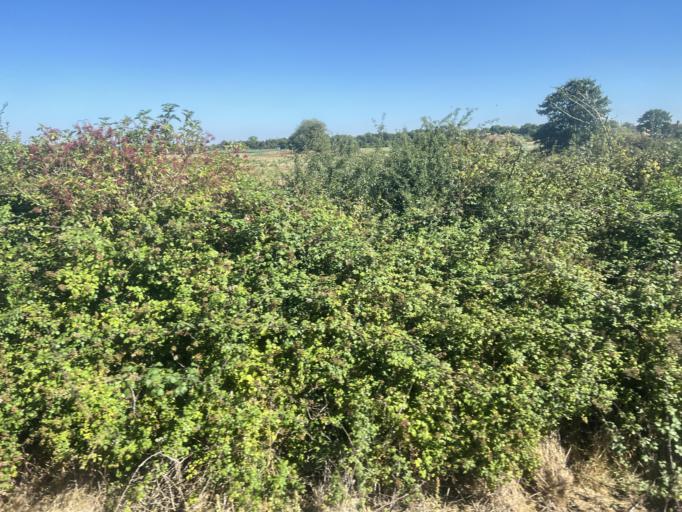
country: GB
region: England
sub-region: Lincolnshire
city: Sleaford
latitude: 52.9914
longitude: -0.3679
